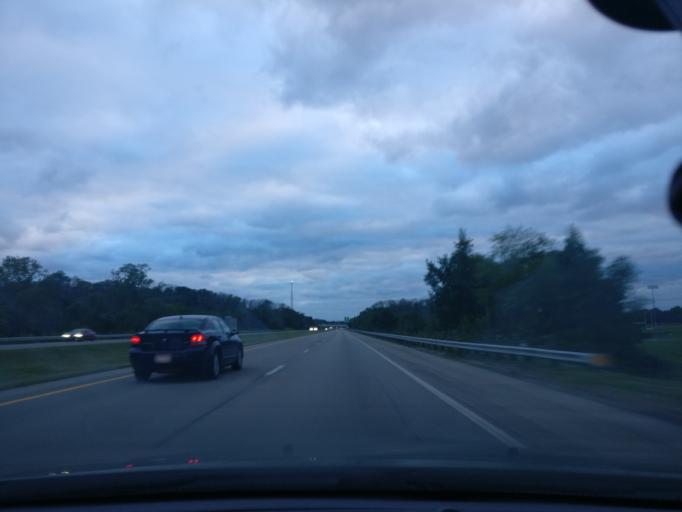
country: US
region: Ohio
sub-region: Greene County
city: Xenia
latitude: 39.6636
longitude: -83.9238
